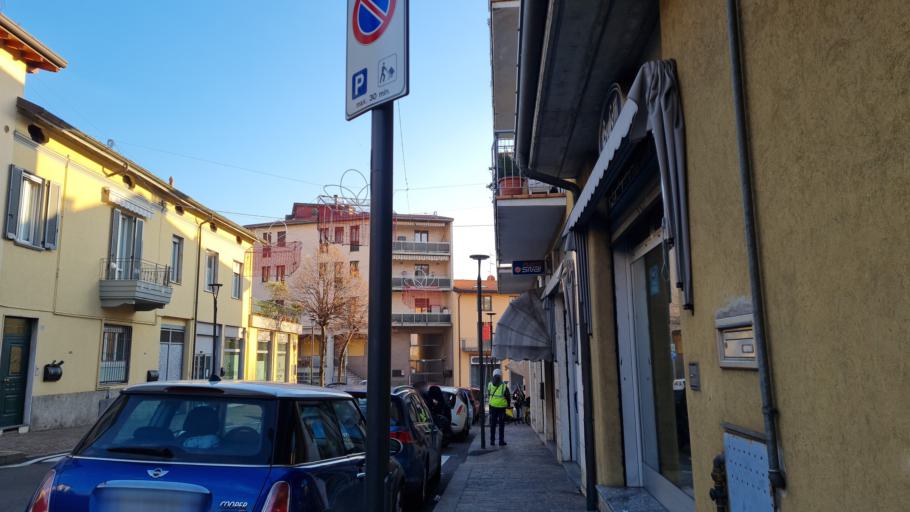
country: IT
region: Lombardy
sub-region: Provincia di Lecco
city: Calolziocorte
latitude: 45.8024
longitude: 9.4332
